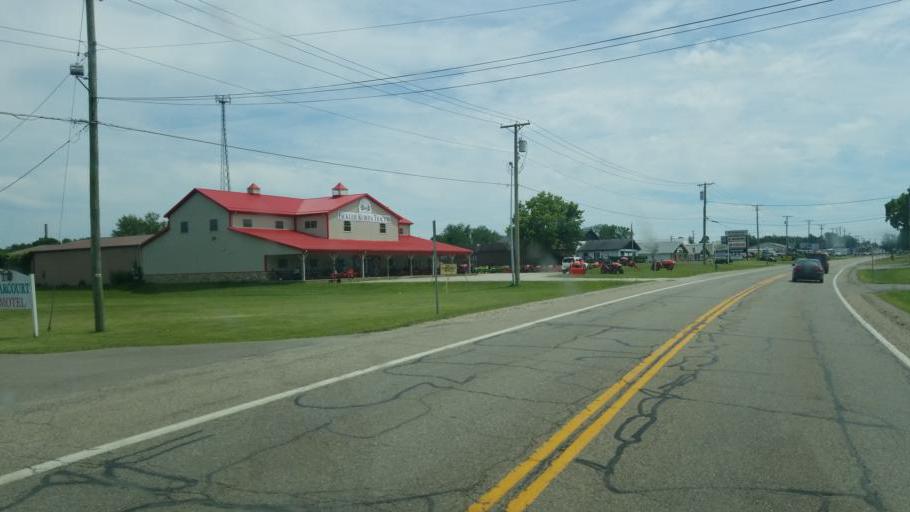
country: US
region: Ohio
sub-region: Knox County
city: Mount Vernon
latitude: 40.3890
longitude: -82.5070
